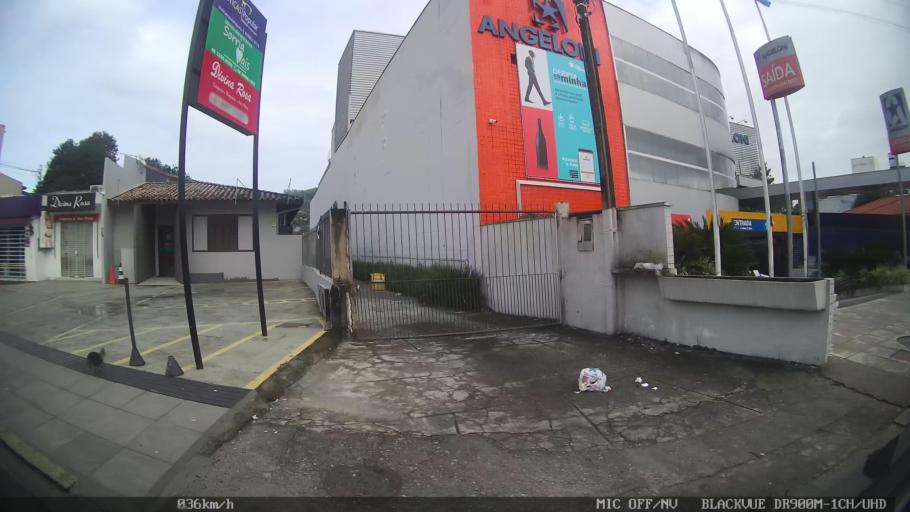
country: BR
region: Santa Catarina
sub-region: Biguacu
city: Biguacu
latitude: -27.4978
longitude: -48.6549
